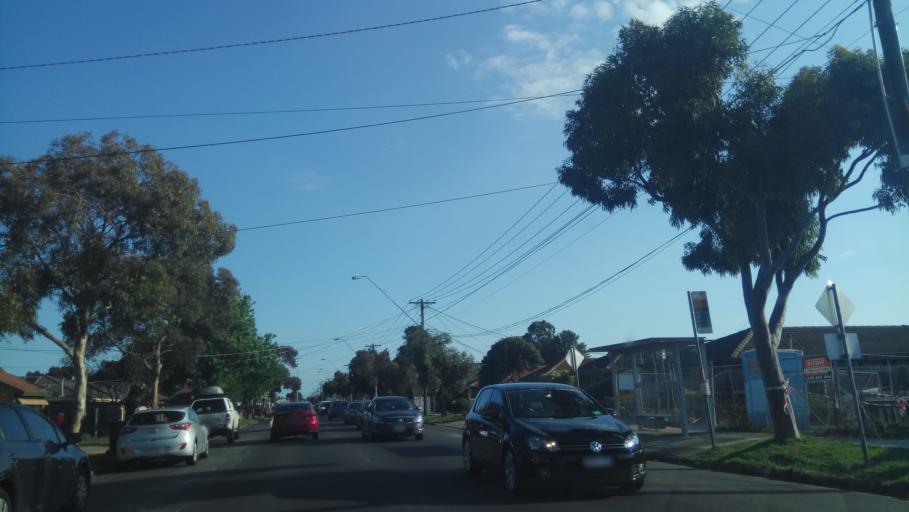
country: AU
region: Victoria
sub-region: Hobsons Bay
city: Laverton
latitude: -37.8694
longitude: 144.7778
